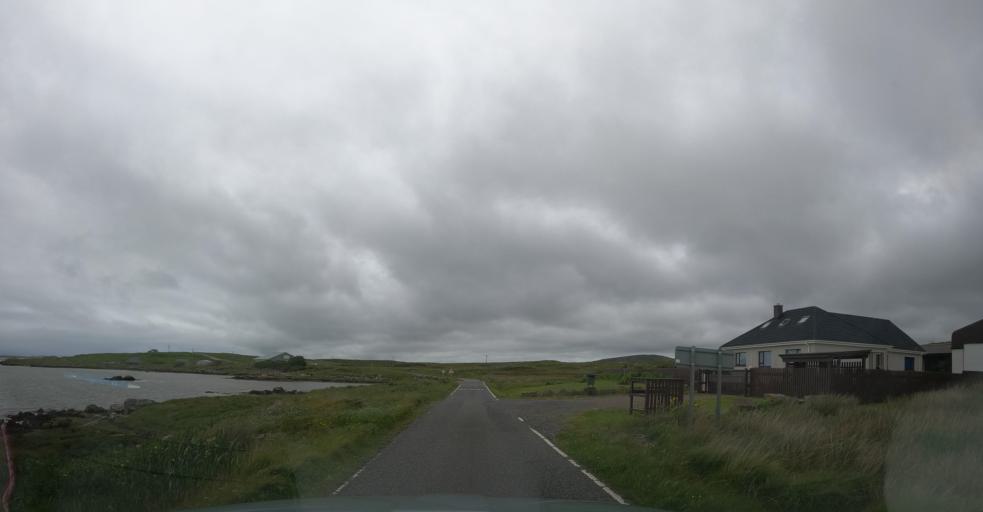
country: GB
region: Scotland
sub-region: Eilean Siar
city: Isle of North Uist
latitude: 57.5542
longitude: -7.3361
